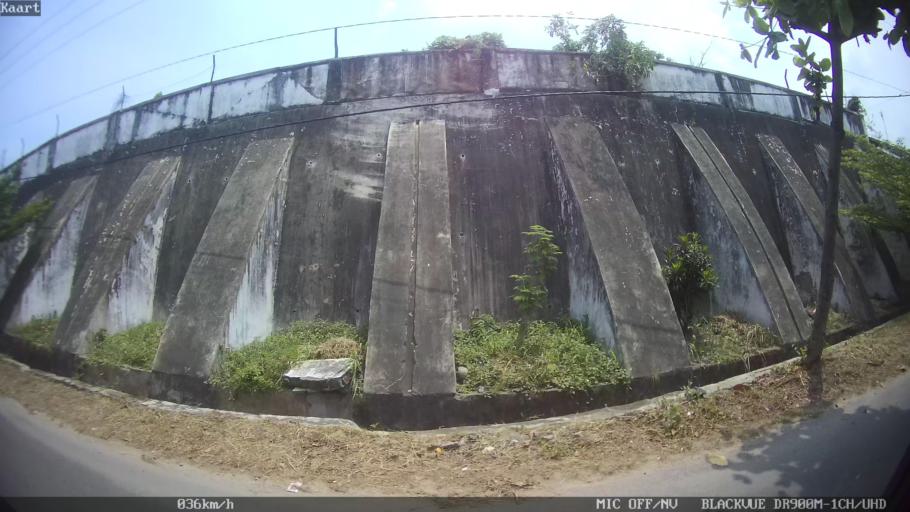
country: ID
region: Lampung
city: Bandarlampung
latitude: -5.4429
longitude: 105.2922
